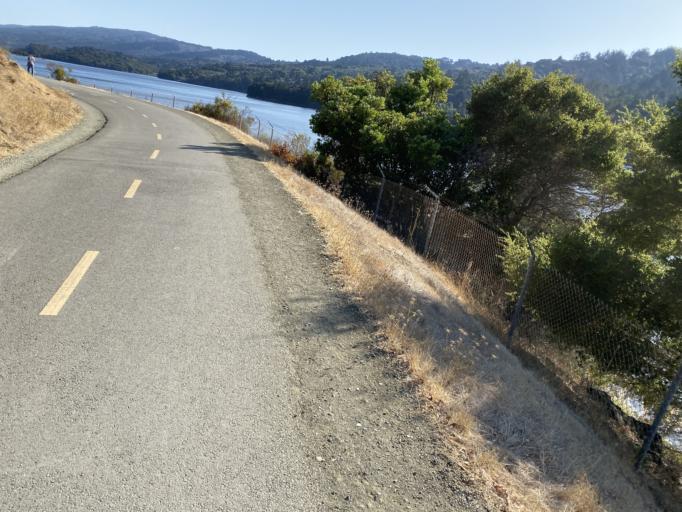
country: US
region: California
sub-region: San Mateo County
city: Highlands-Baywood Park
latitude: 37.5319
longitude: -122.3665
